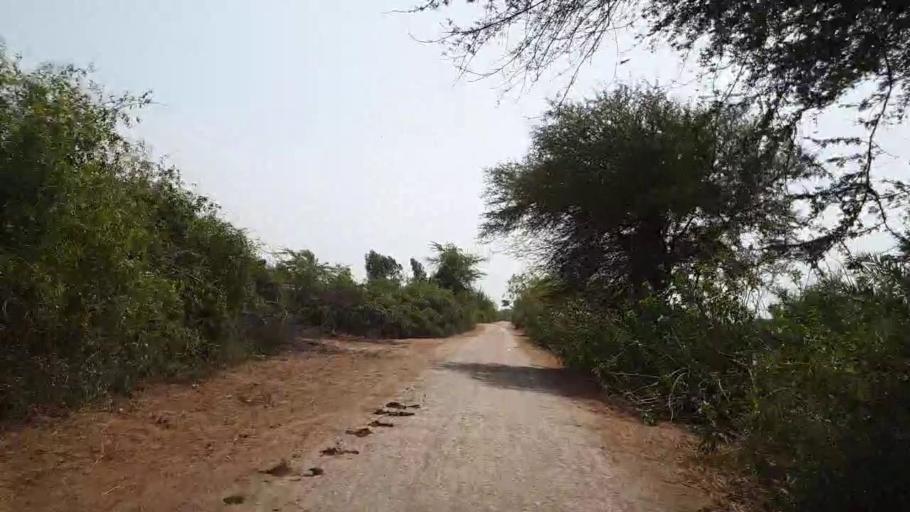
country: PK
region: Sindh
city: Matli
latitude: 25.0344
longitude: 68.7038
